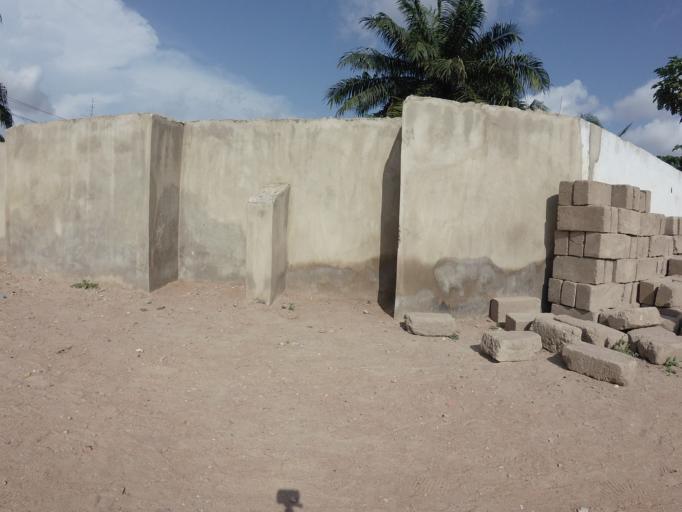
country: GH
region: Greater Accra
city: Dome
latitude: 5.6164
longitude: -0.2370
